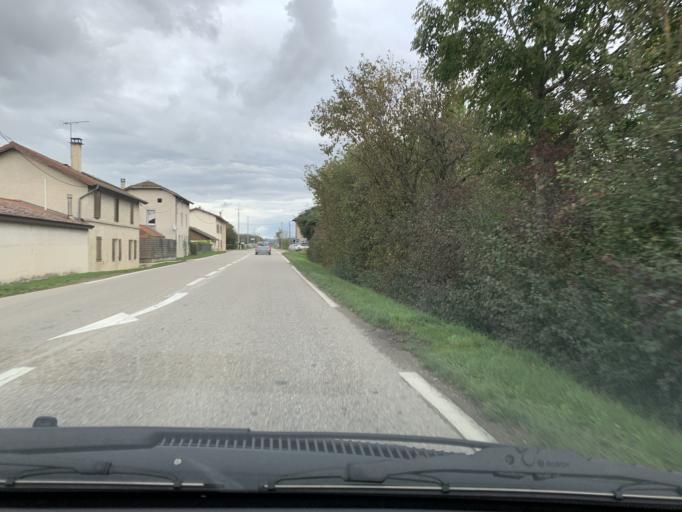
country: FR
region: Rhone-Alpes
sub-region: Departement de l'Isere
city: Chatte
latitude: 45.1274
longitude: 5.2844
